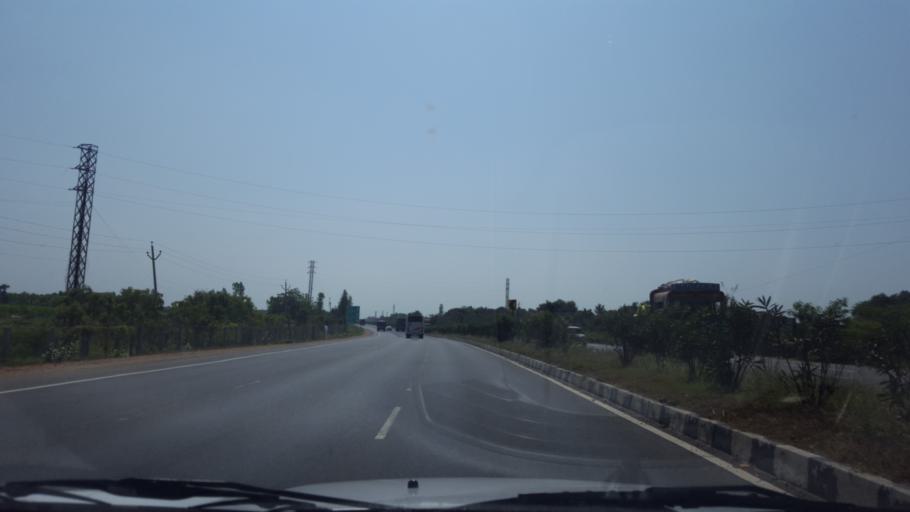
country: IN
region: Andhra Pradesh
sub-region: Prakasam
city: Ongole
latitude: 15.6330
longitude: 80.0167
